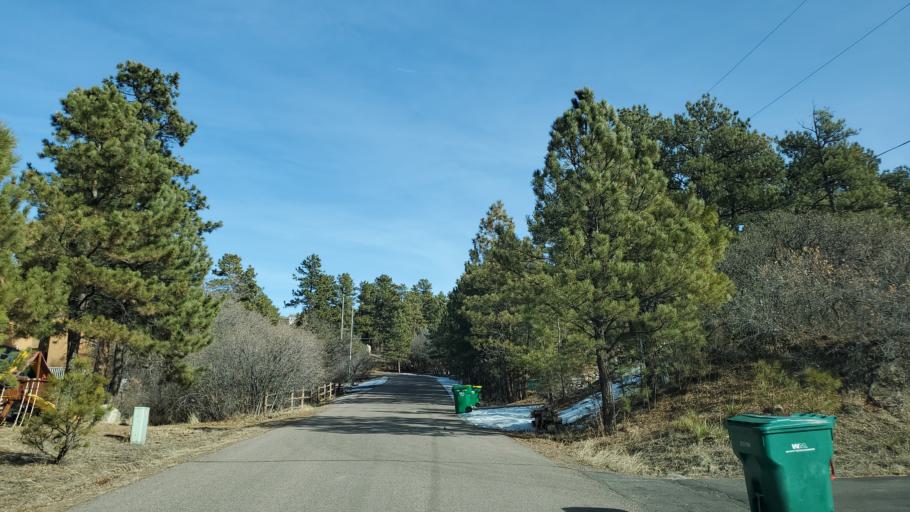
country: US
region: Colorado
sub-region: Douglas County
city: Castle Pines
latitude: 39.4272
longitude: -104.8744
